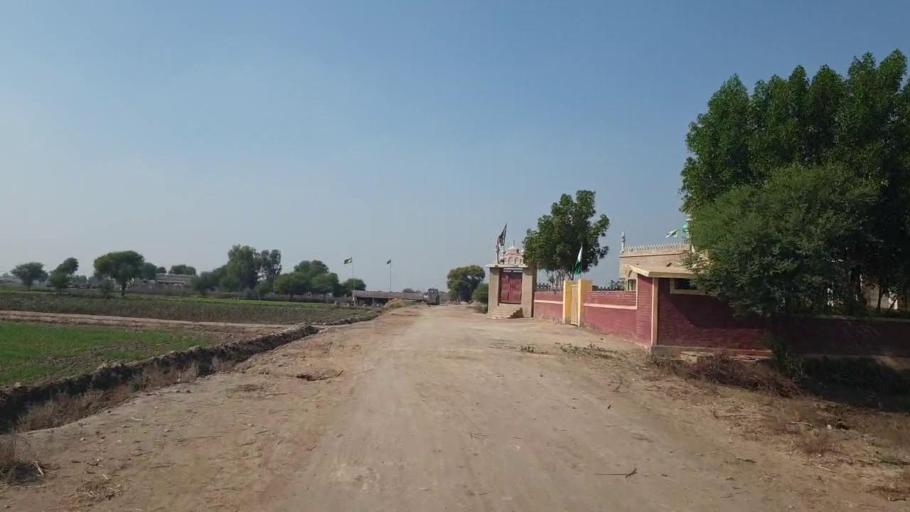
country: PK
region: Sindh
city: Sehwan
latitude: 26.4293
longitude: 67.8191
